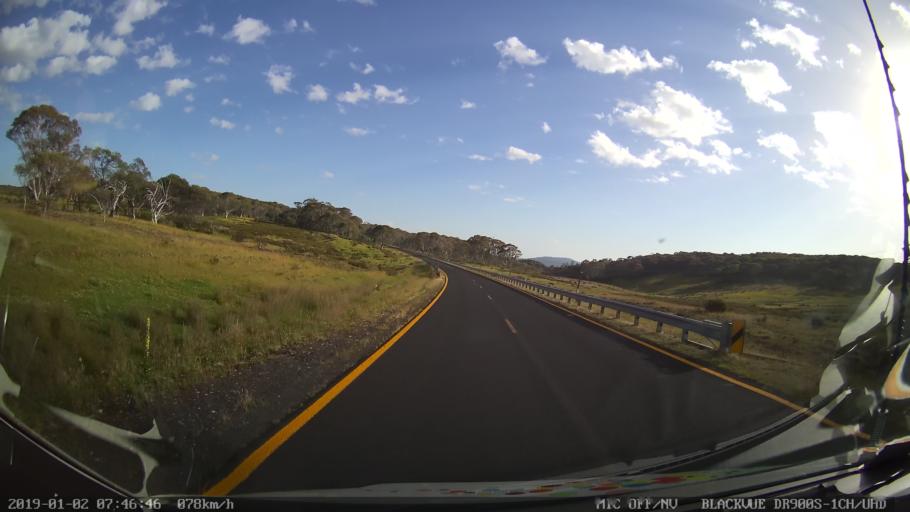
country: AU
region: New South Wales
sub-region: Tumut Shire
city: Tumut
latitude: -35.7720
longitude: 148.5199
